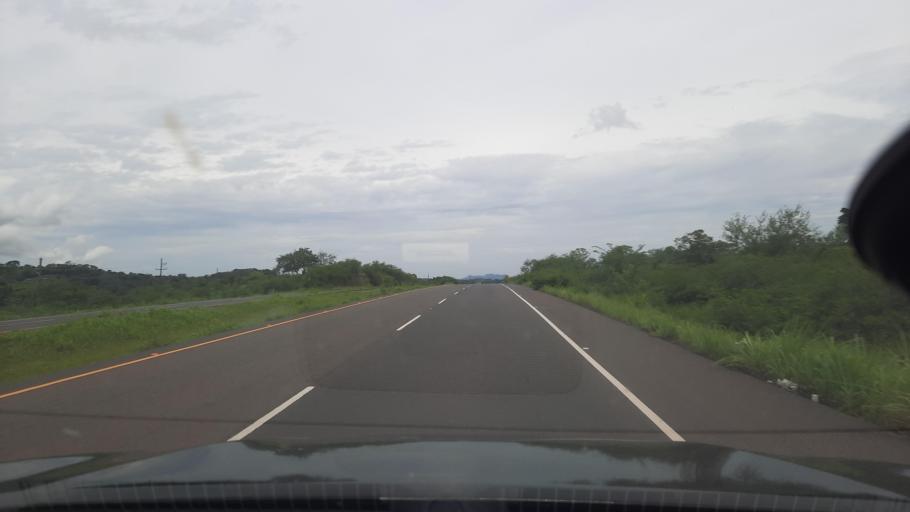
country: HN
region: Valle
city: Aramecina
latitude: 13.7734
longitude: -87.7006
